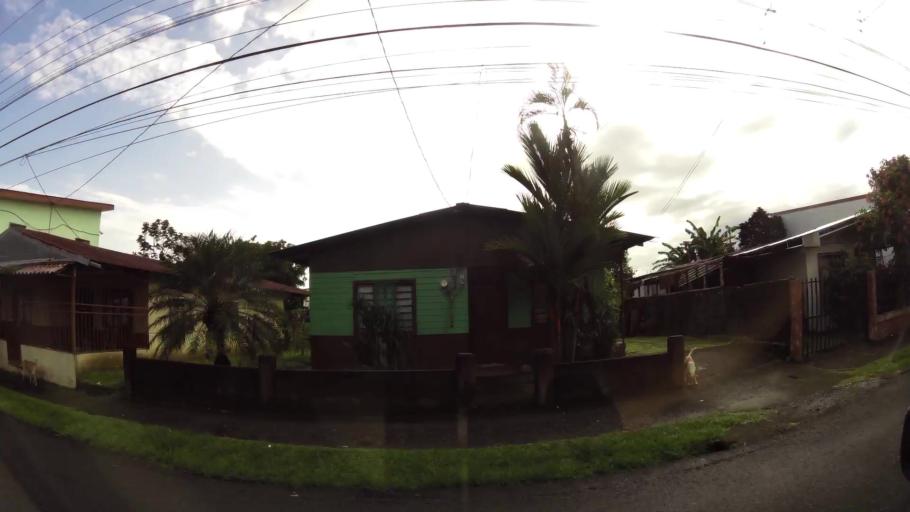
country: CR
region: Limon
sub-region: Canton de Guacimo
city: Guacimo
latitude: 10.2111
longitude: -83.6810
